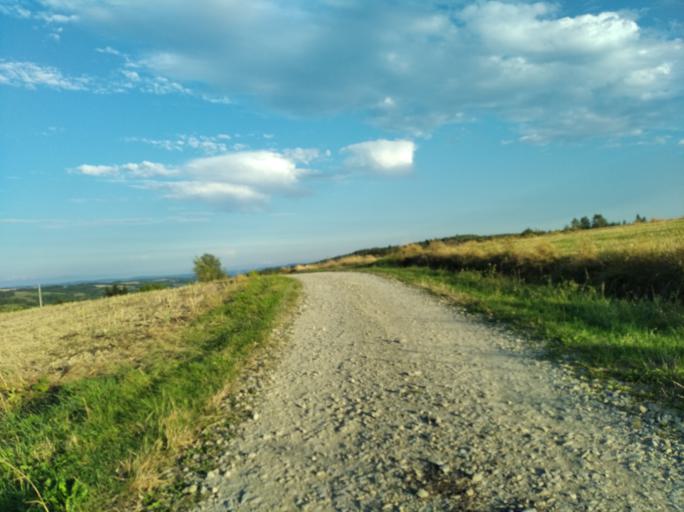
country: PL
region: Subcarpathian Voivodeship
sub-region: Powiat ropczycko-sedziszowski
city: Wielopole Skrzynskie
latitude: 49.9129
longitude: 21.5978
